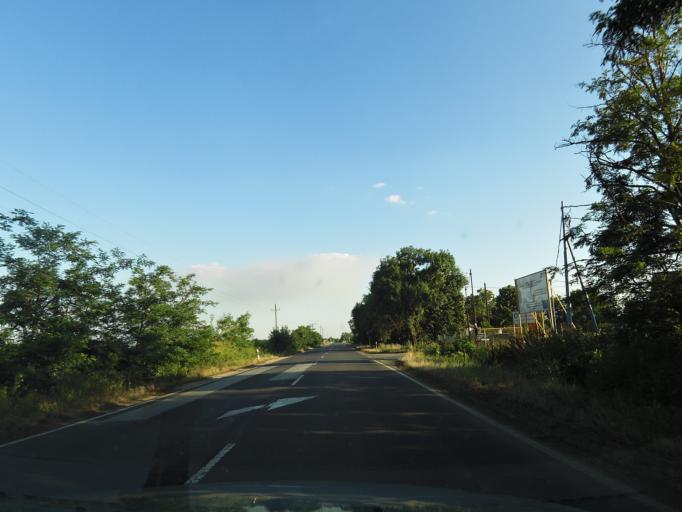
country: HU
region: Jasz-Nagykun-Szolnok
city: Kunszentmarton
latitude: 46.8624
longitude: 20.2656
